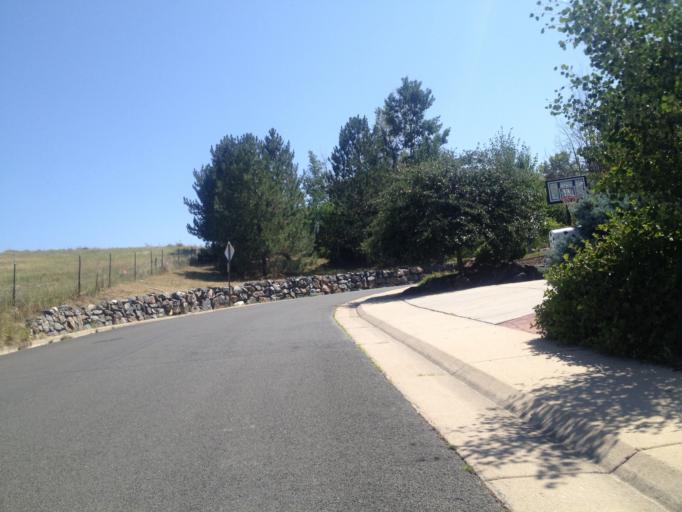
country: US
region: Colorado
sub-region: Boulder County
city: Louisville
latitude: 39.9612
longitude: -105.1422
